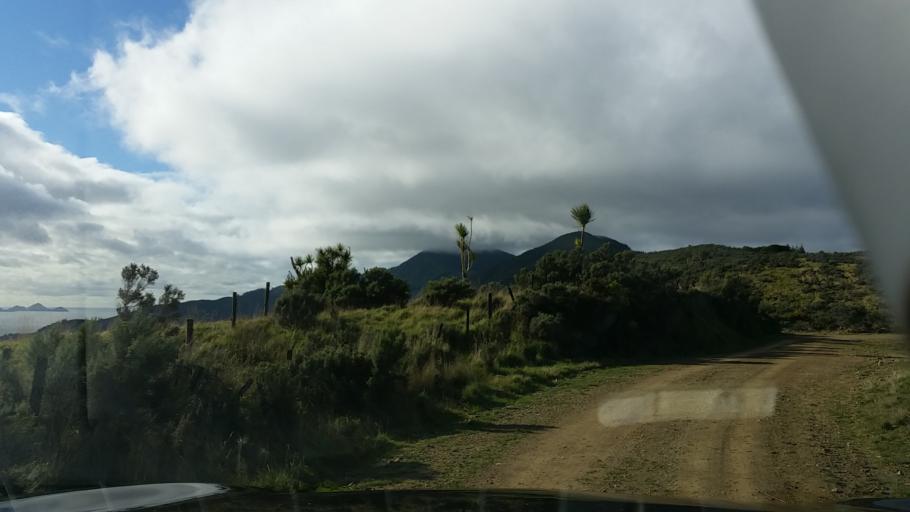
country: NZ
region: Marlborough
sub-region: Marlborough District
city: Picton
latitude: -40.9674
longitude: 173.8923
